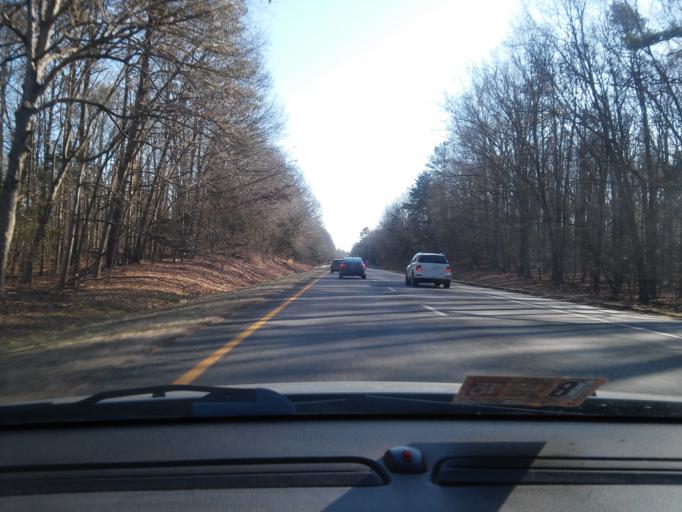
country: US
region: Virginia
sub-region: Henrico County
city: Wyndham
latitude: 37.6972
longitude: -77.7283
